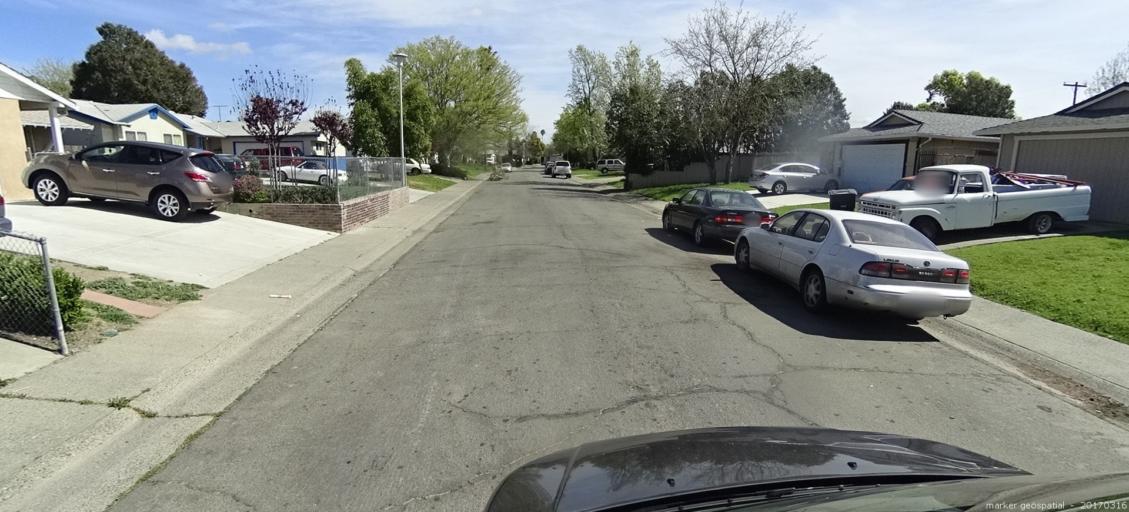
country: US
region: California
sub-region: Sacramento County
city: Parkway
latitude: 38.4787
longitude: -121.4856
